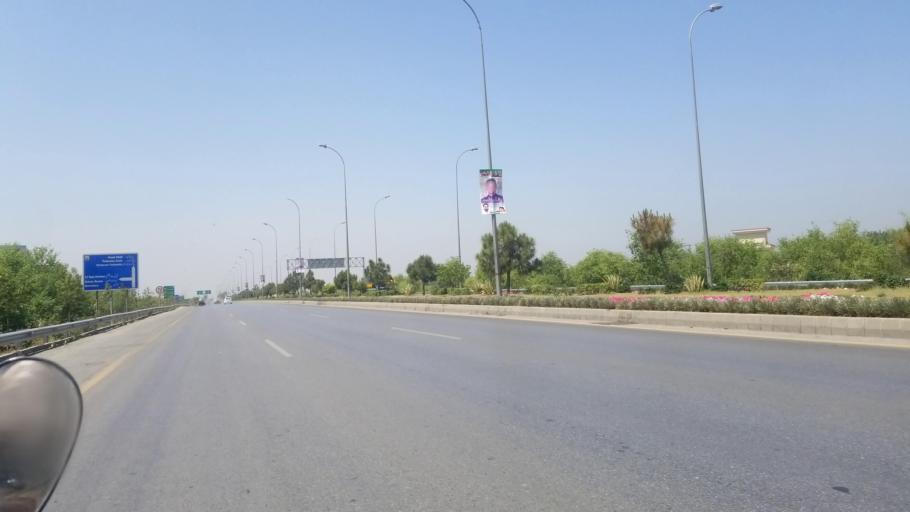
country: PK
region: Khyber Pakhtunkhwa
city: Peshawar
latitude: 34.0275
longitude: 71.6539
